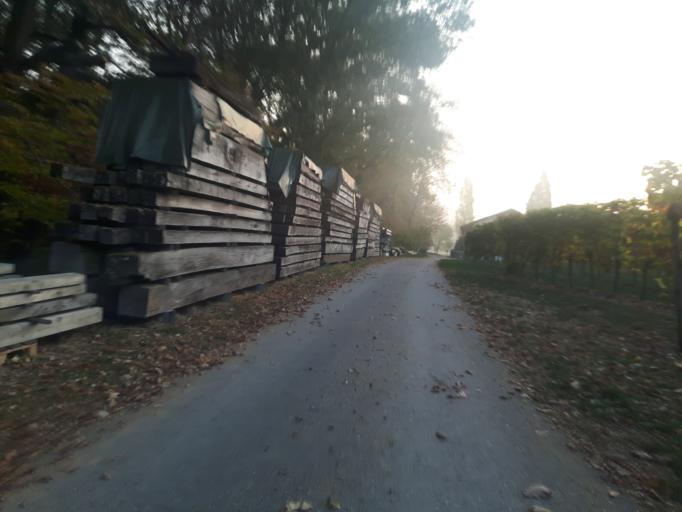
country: DE
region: Baden-Wuerttemberg
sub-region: Regierungsbezirk Stuttgart
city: Beilstein
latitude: 49.0652
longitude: 9.3243
